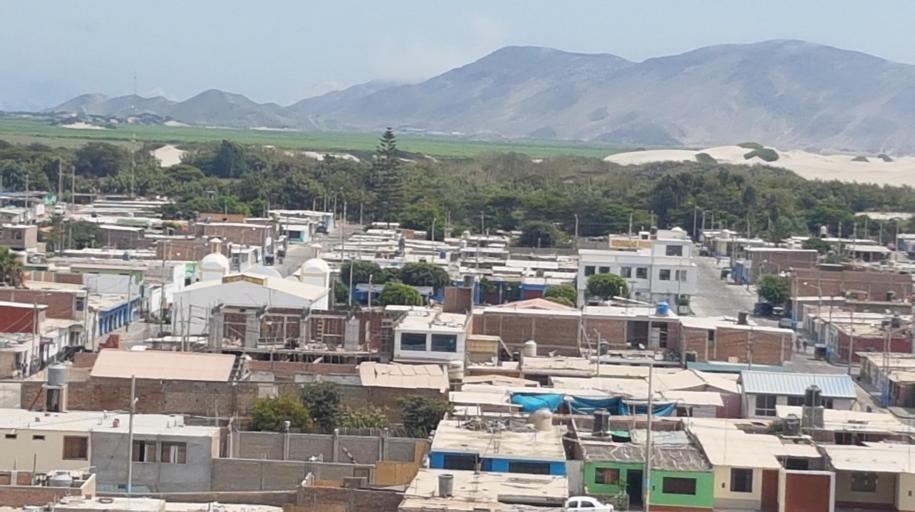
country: PE
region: Ancash
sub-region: Provincia de Santa
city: Samanco
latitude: -9.2587
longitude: -78.4966
